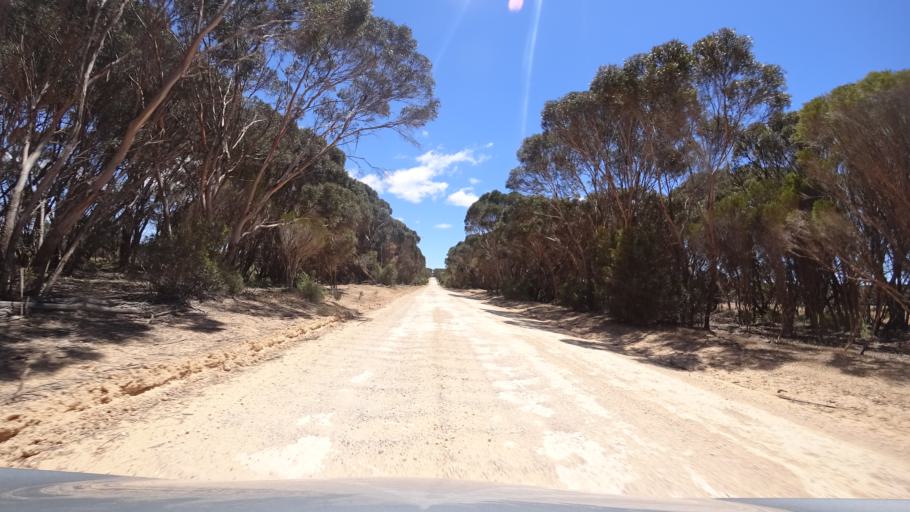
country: AU
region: South Australia
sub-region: Yankalilla
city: Normanville
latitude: -35.8249
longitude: 138.0811
